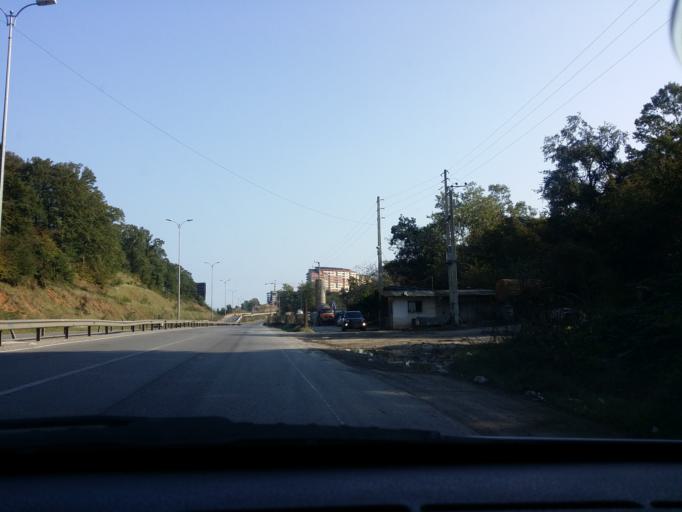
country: IR
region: Mazandaran
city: Chalus
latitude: 36.6400
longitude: 51.4156
